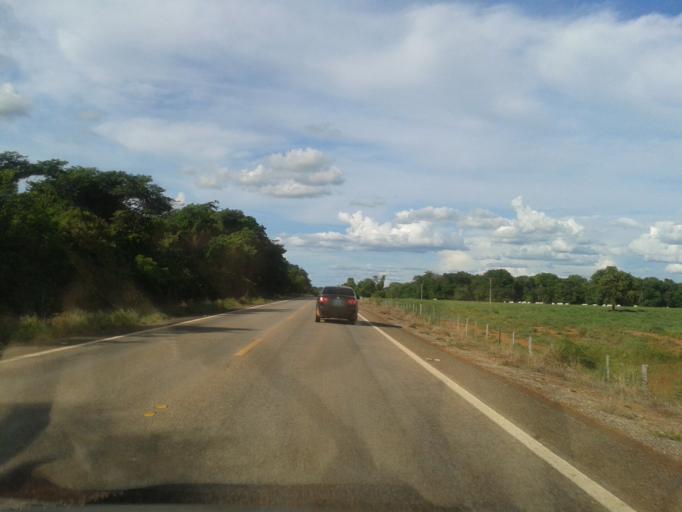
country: BR
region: Goias
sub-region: Mozarlandia
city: Mozarlandia
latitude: -14.3186
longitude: -50.4089
